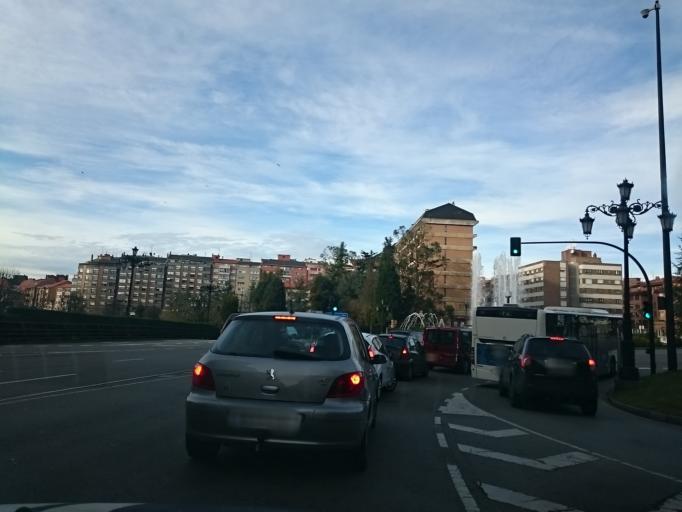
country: ES
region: Asturias
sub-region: Province of Asturias
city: Oviedo
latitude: 43.3604
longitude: -5.8495
